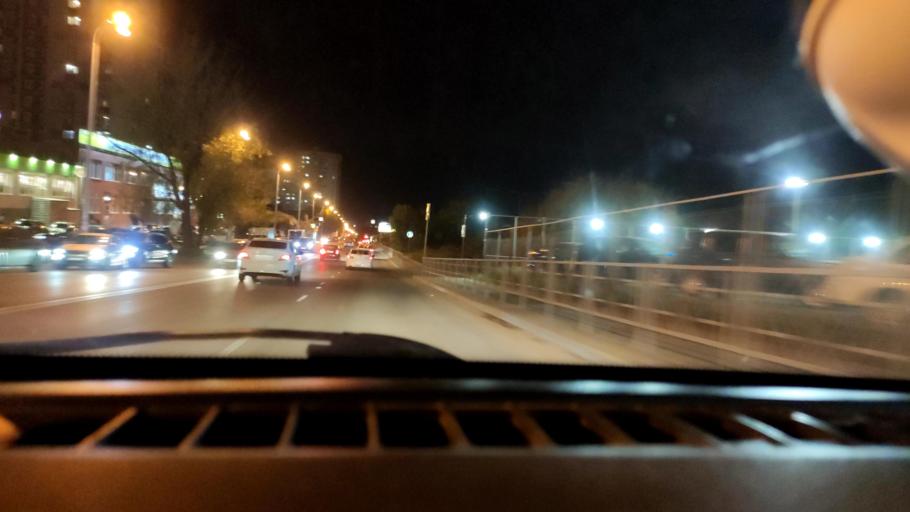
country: RU
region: Samara
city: Samara
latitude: 53.2062
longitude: 50.2058
